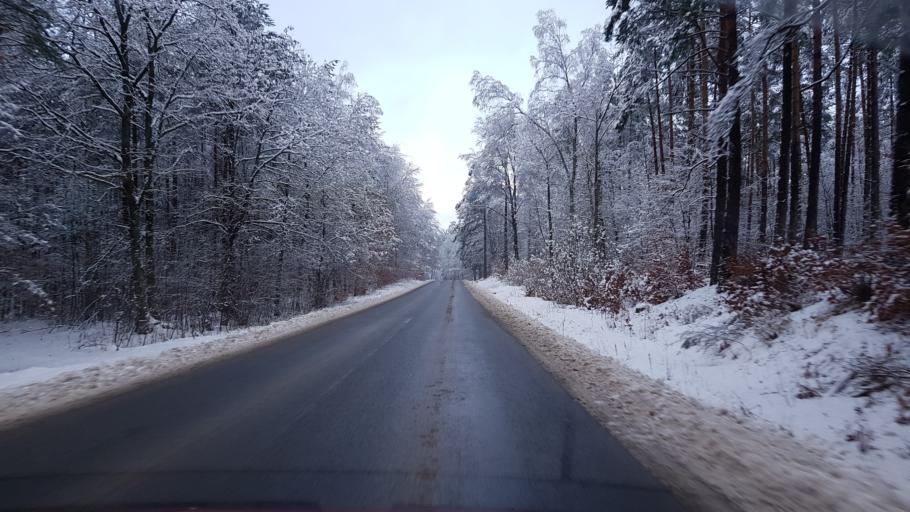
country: PL
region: West Pomeranian Voivodeship
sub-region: Powiat drawski
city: Zlocieniec
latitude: 53.5597
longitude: 16.0108
